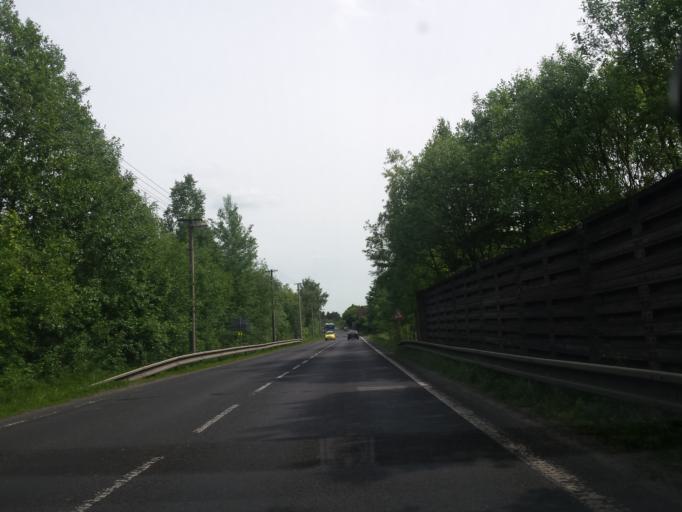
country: CZ
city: Novy Bor
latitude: 50.7472
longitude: 14.5501
